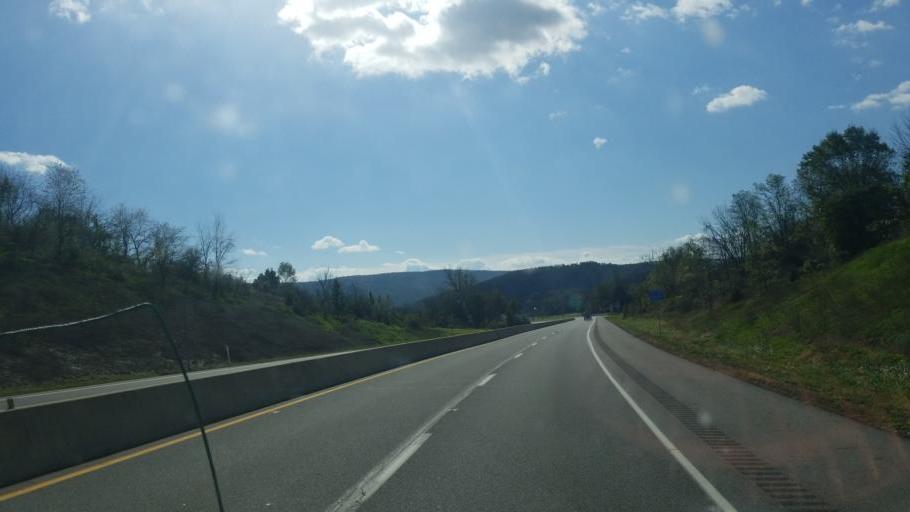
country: US
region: Pennsylvania
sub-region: Bedford County
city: Bedford
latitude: 40.0326
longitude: -78.5173
